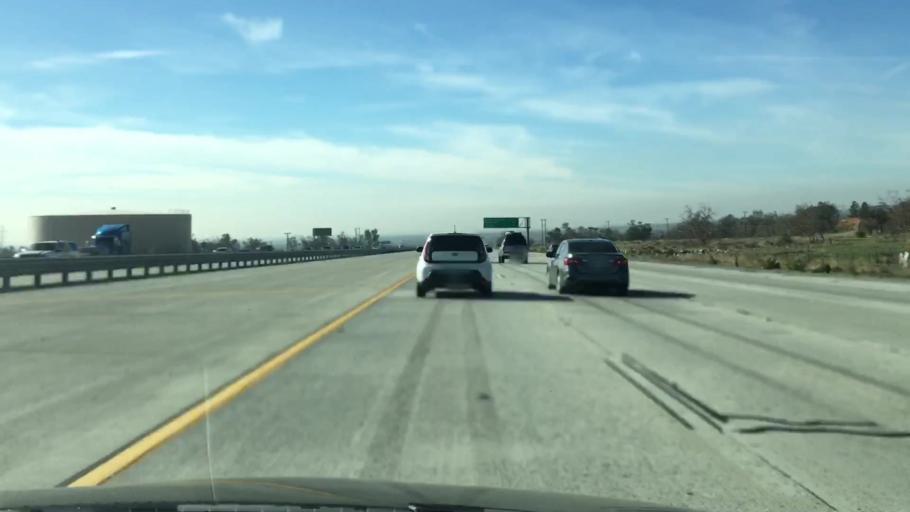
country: US
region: California
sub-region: San Bernardino County
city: Fontana
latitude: 34.1742
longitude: -117.4484
